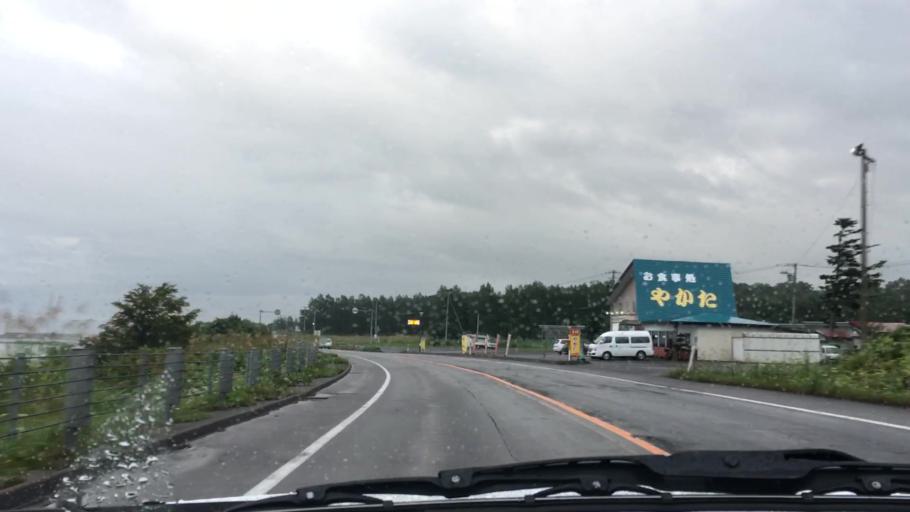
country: JP
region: Hokkaido
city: Nanae
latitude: 42.1791
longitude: 140.4428
